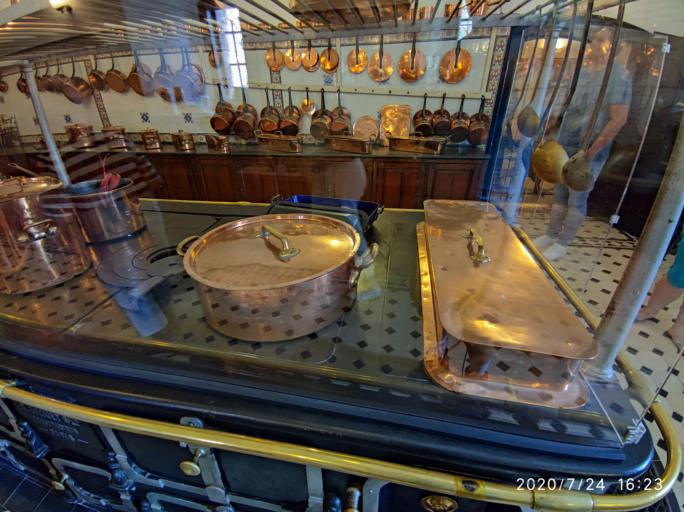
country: NL
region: Utrecht
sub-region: Stichtse Vecht
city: Spechtenkamp
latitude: 52.1211
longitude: 4.9921
